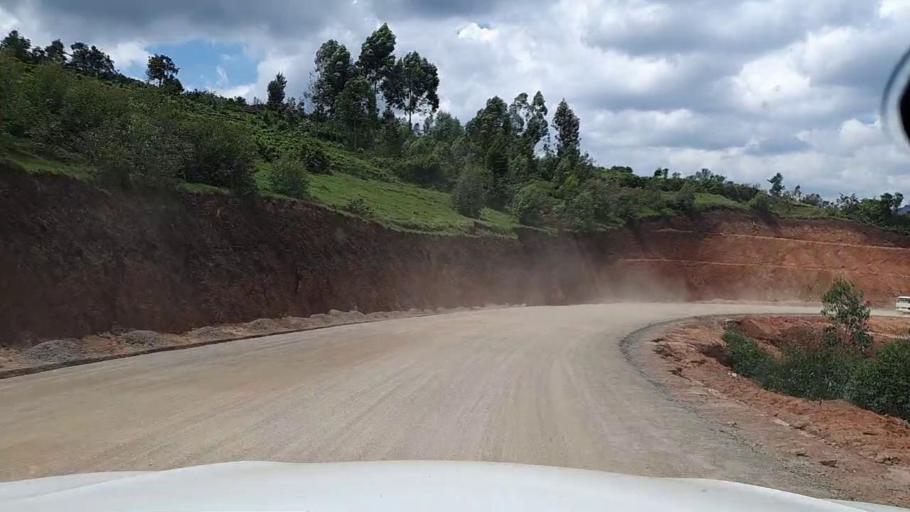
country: RW
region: Southern Province
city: Butare
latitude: -2.6942
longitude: 29.5577
